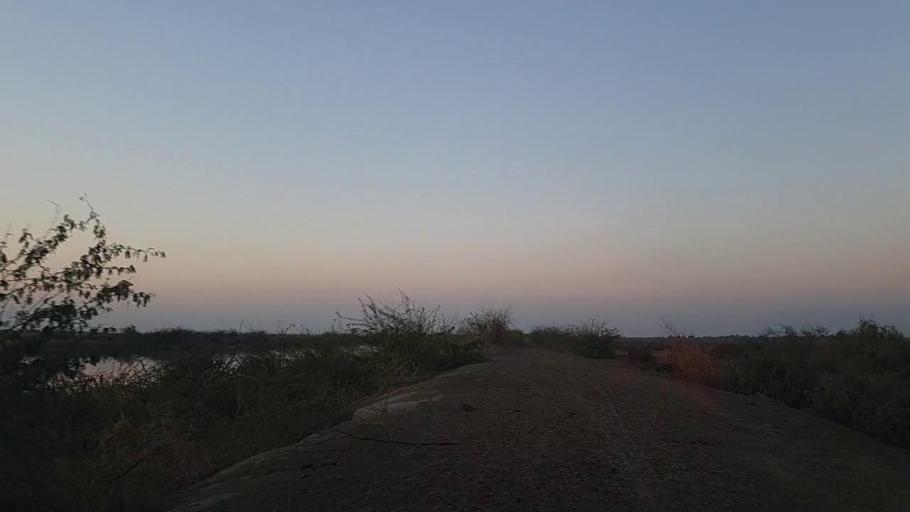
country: PK
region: Sindh
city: Tando Mittha Khan
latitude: 26.0745
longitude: 69.1545
